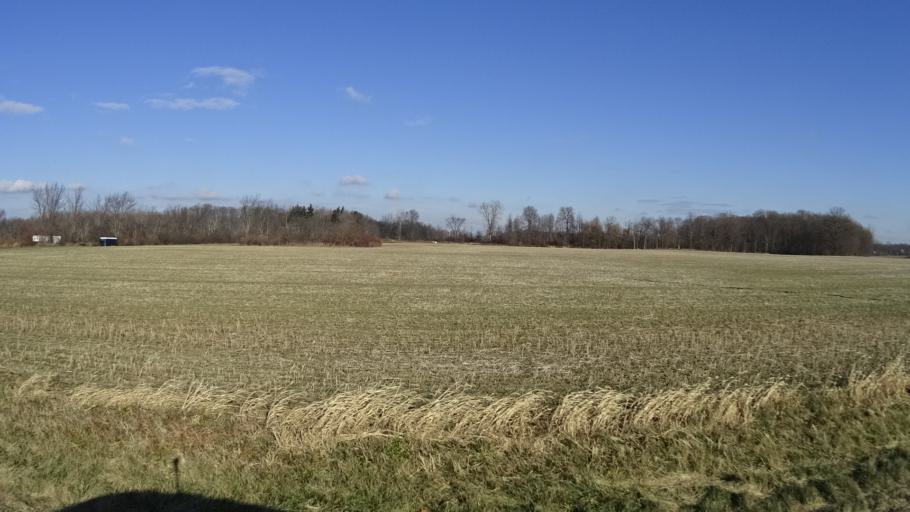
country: US
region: Ohio
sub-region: Lorain County
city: Wellington
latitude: 41.2237
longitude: -82.1874
